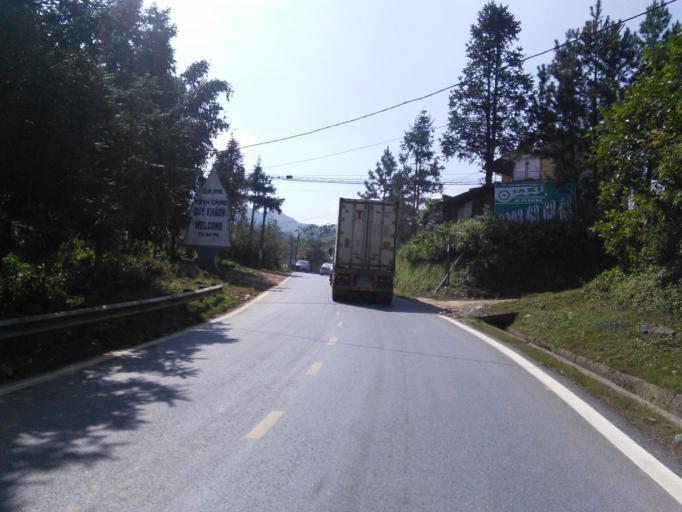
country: VN
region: Lao Cai
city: Sa Pa
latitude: 22.3532
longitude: 103.8603
